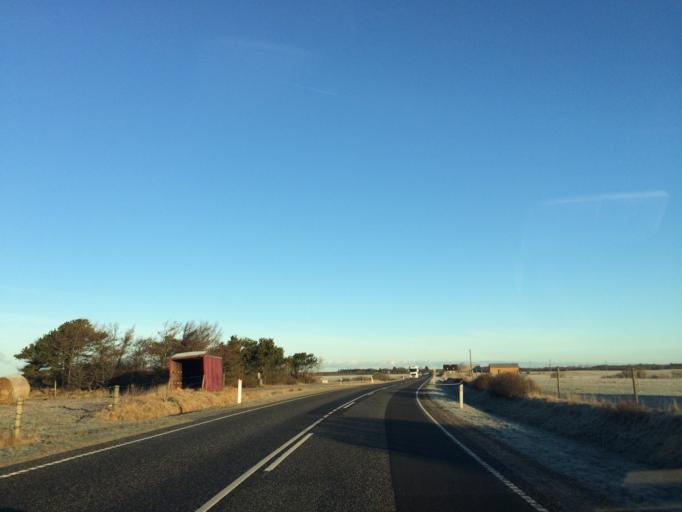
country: DK
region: Central Jutland
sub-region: Lemvig Kommune
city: Lemvig
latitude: 56.4350
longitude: 8.2976
